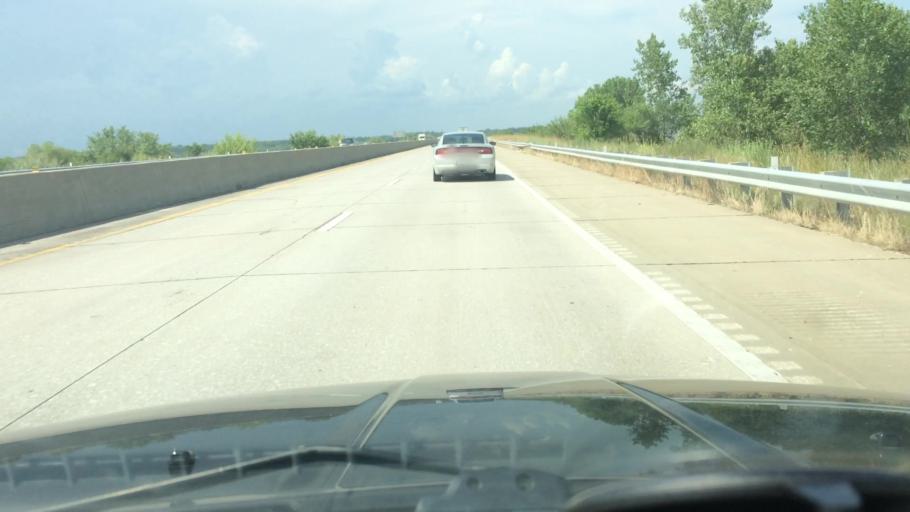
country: US
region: Missouri
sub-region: Henry County
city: Clinton
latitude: 38.2689
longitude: -93.7600
